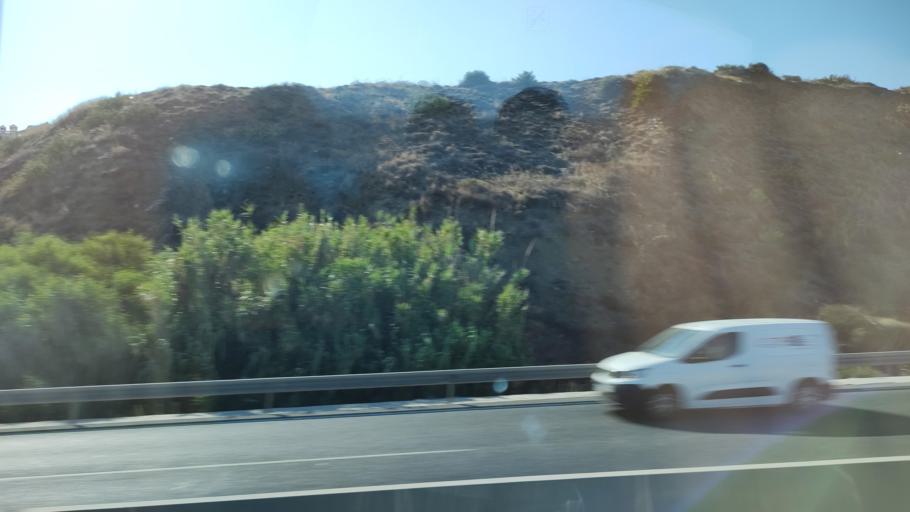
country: ES
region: Andalusia
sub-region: Provincia de Malaga
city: Fuengirola
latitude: 36.5128
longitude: -4.6349
